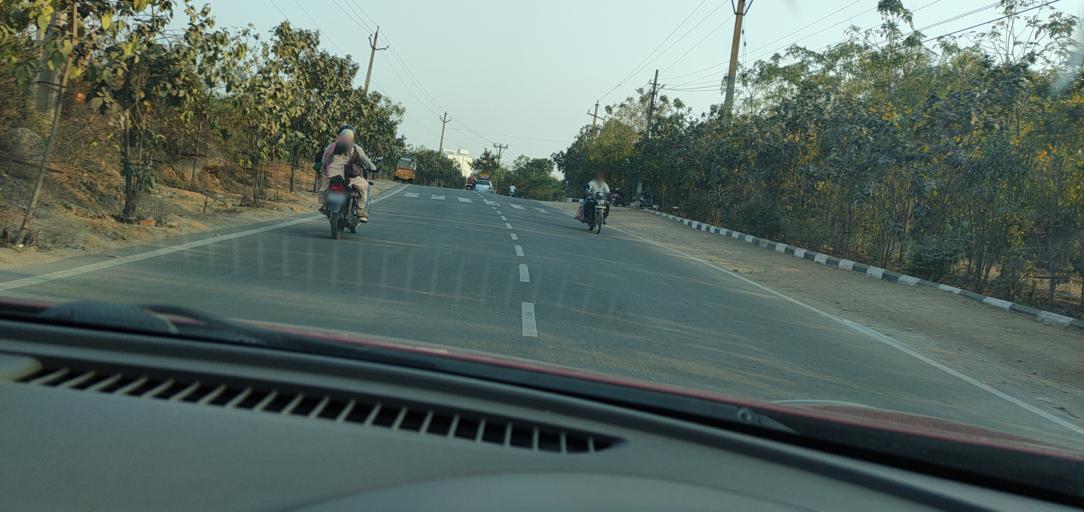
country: IN
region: Telangana
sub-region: Rangareddi
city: Uppal Kalan
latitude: 17.4314
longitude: 78.5787
